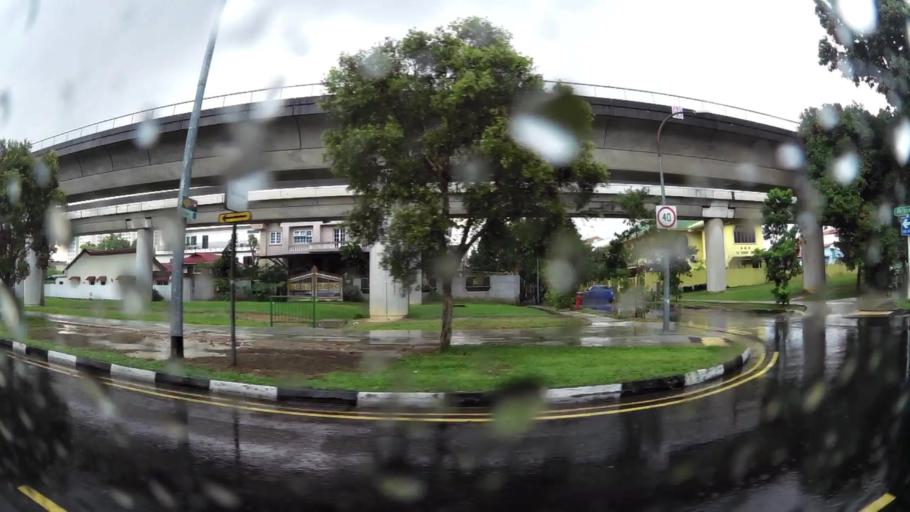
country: SG
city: Singapore
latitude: 1.3212
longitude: 103.9146
